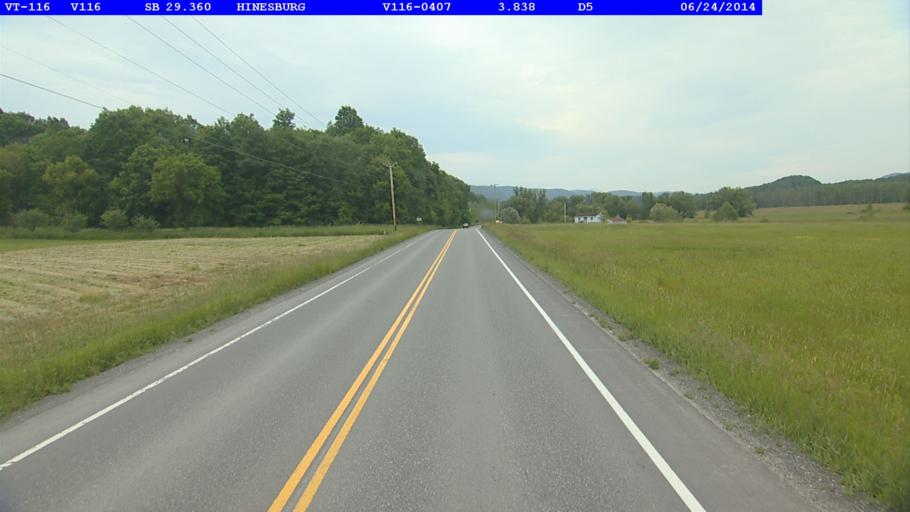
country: US
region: Vermont
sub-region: Chittenden County
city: Hinesburg
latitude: 44.3244
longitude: -73.1003
